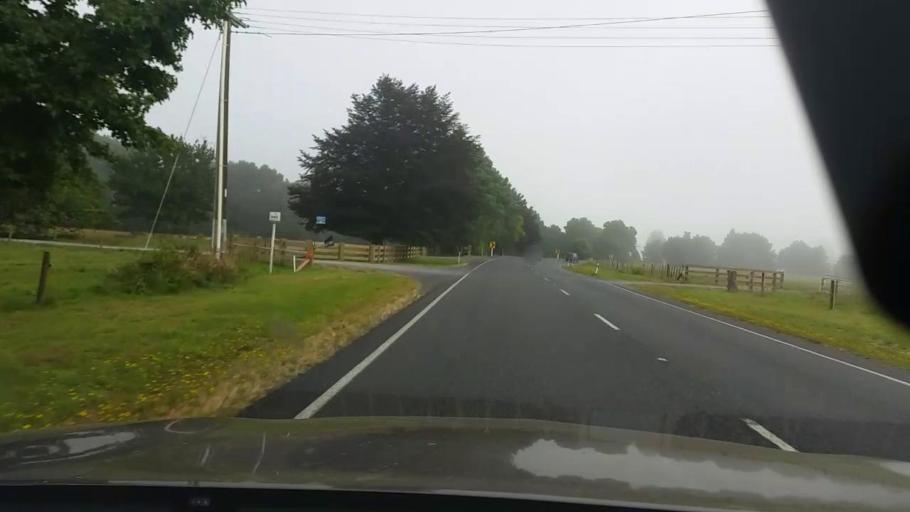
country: NZ
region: Waikato
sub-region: Hamilton City
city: Hamilton
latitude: -37.6422
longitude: 175.2949
